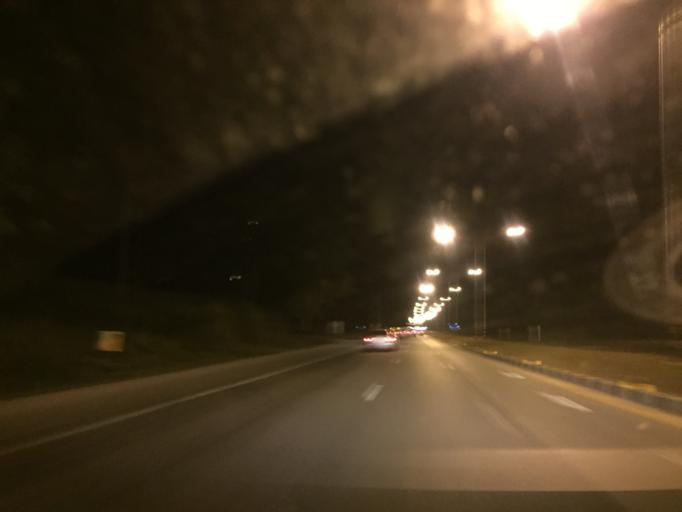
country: TH
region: Changwat Udon Thani
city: Nong Wua So
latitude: 17.2453
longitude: 102.5378
